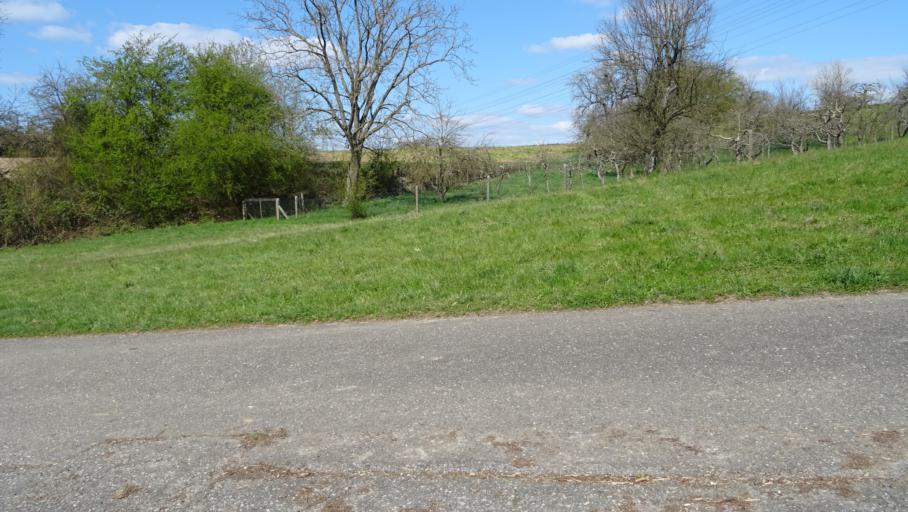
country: DE
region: Baden-Wuerttemberg
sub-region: Karlsruhe Region
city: Neckarzimmern
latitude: 49.3324
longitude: 9.1148
